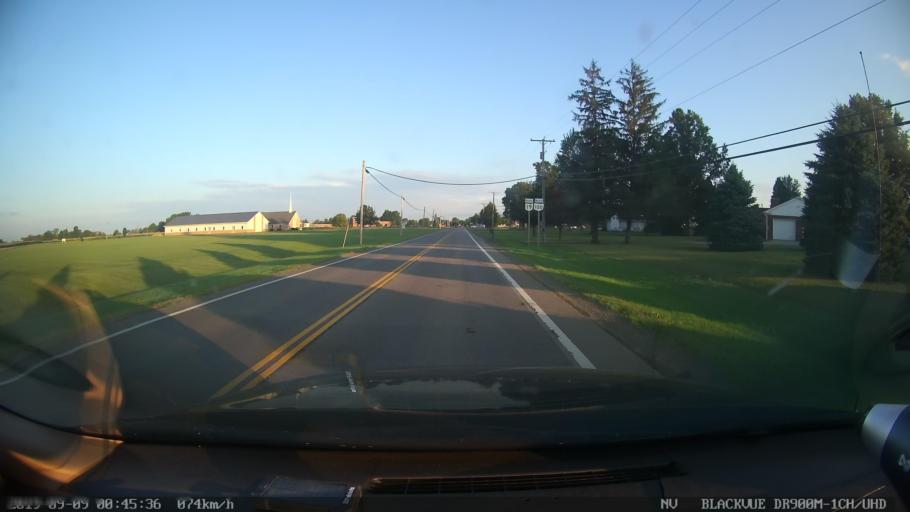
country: US
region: Ohio
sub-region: Crawford County
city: Bucyrus
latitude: 40.7888
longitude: -82.9466
